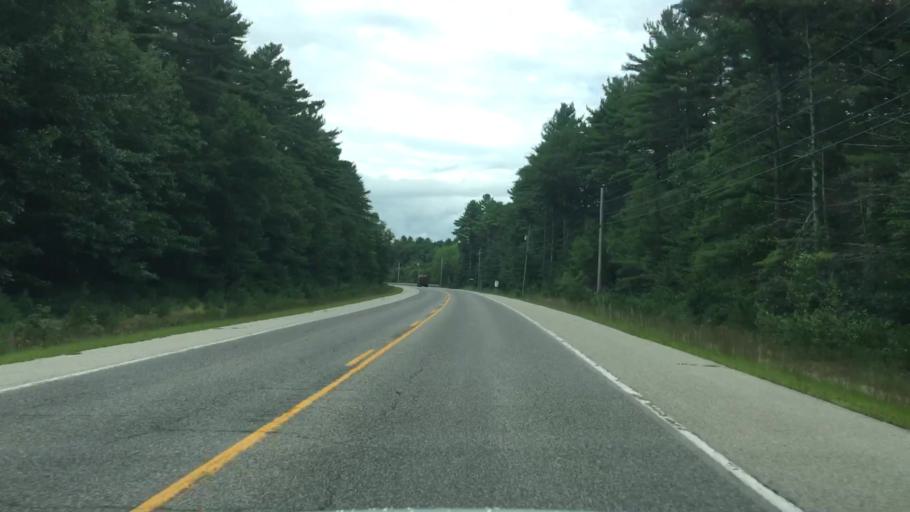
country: US
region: Maine
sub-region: York County
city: North Berwick
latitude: 43.3520
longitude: -70.7285
